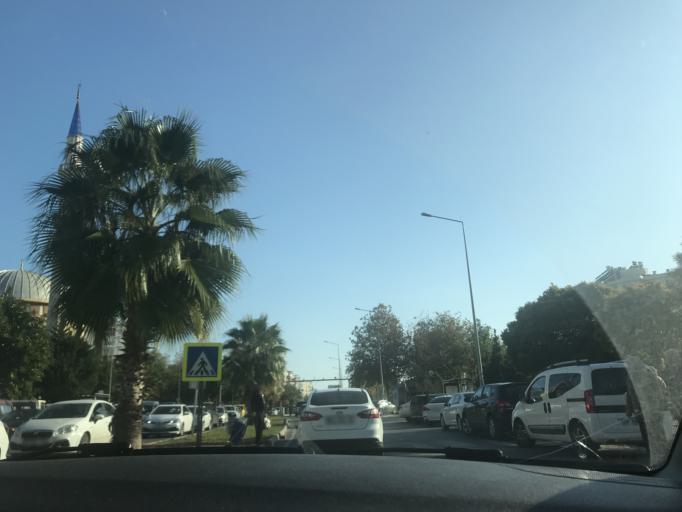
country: TR
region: Antalya
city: Antalya
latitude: 36.8827
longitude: 30.6486
